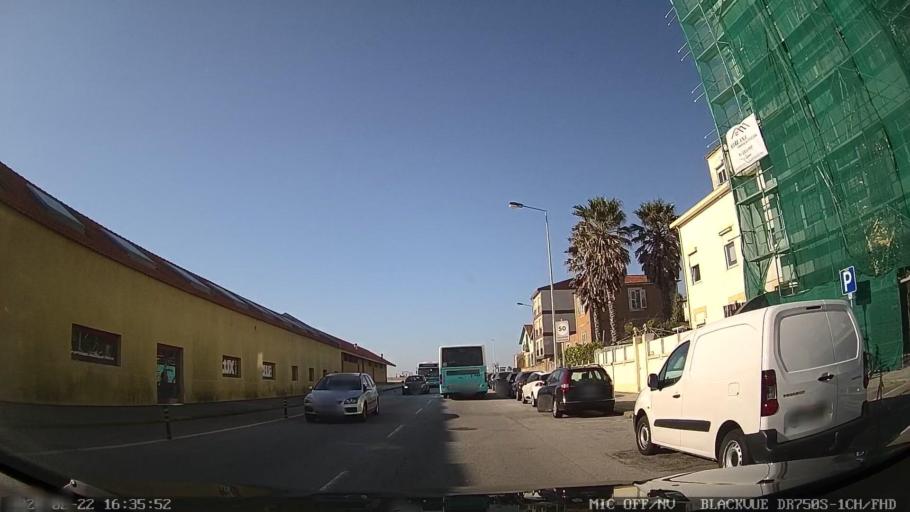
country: PT
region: Porto
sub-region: Matosinhos
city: Leca da Palmeira
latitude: 41.1886
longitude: -8.7038
